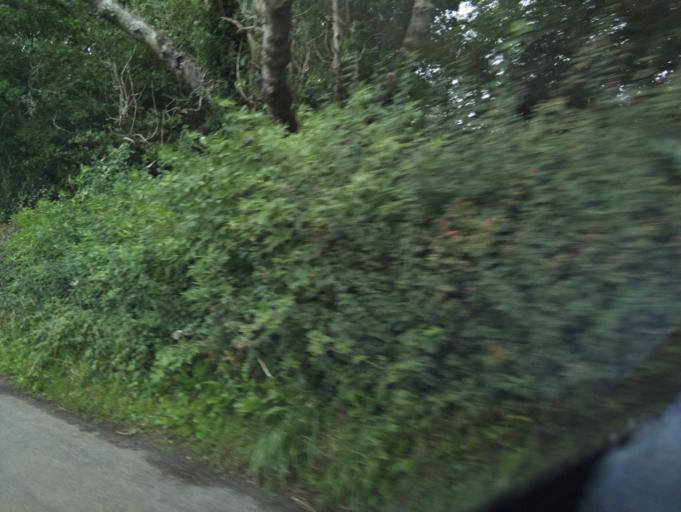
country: GB
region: England
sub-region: Somerset
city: Evercreech
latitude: 51.1682
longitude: -2.5063
